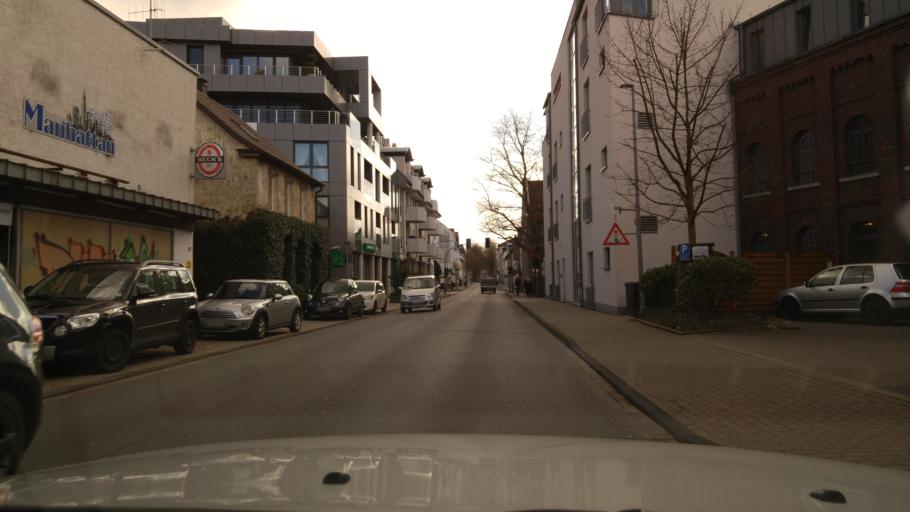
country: DE
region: North Rhine-Westphalia
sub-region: Regierungsbezirk Arnsberg
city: Menden
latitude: 51.4363
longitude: 7.7990
